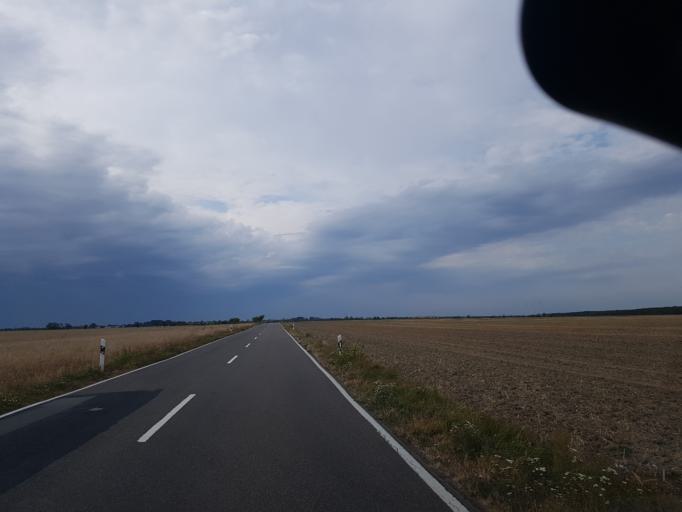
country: DE
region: Saxony
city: Strehla
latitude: 51.3837
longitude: 13.2800
